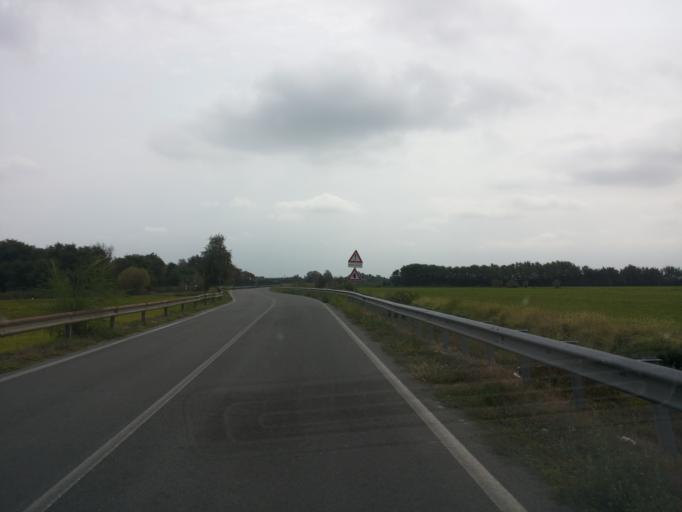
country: IT
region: Piedmont
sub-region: Provincia di Vercelli
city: Prarolo
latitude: 45.2996
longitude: 8.4619
